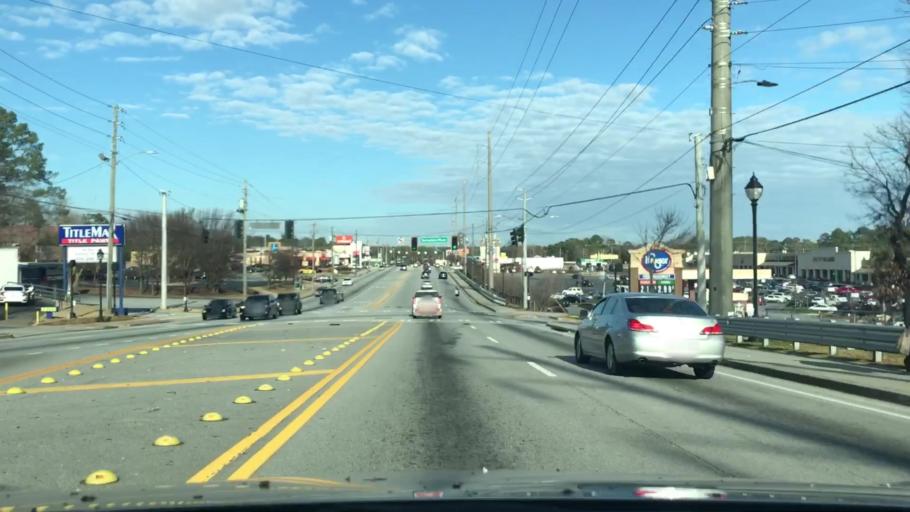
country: US
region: Georgia
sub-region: DeKalb County
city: Belvedere Park
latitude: 33.7523
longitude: -84.2712
